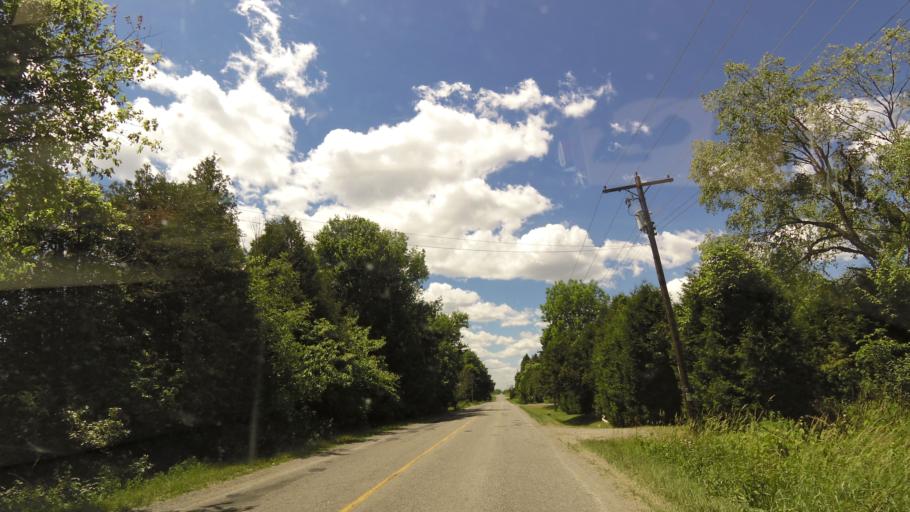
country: CA
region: Ontario
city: Omemee
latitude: 43.9733
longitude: -78.5124
